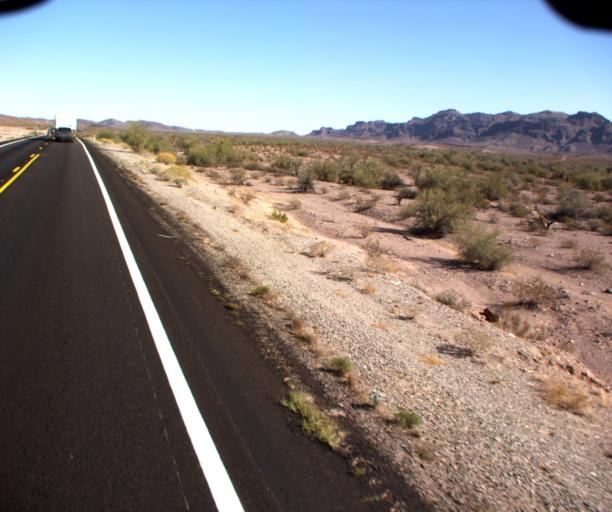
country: US
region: Arizona
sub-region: La Paz County
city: Quartzsite
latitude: 33.1734
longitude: -114.2764
